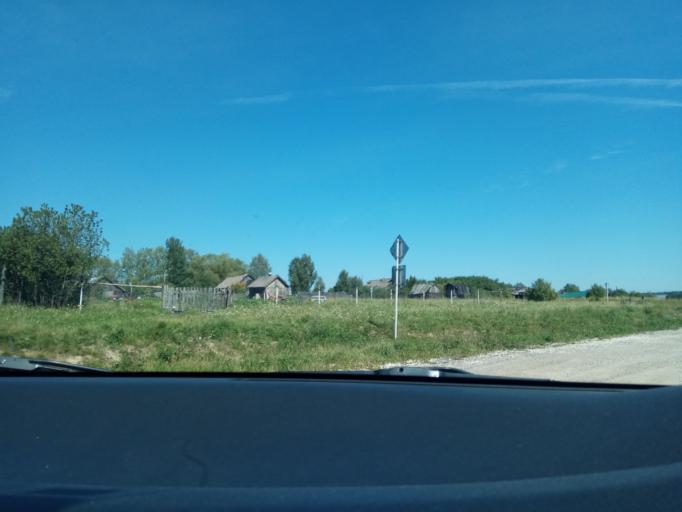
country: RU
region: Vladimir
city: Dobryatino
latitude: 55.7671
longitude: 41.4129
